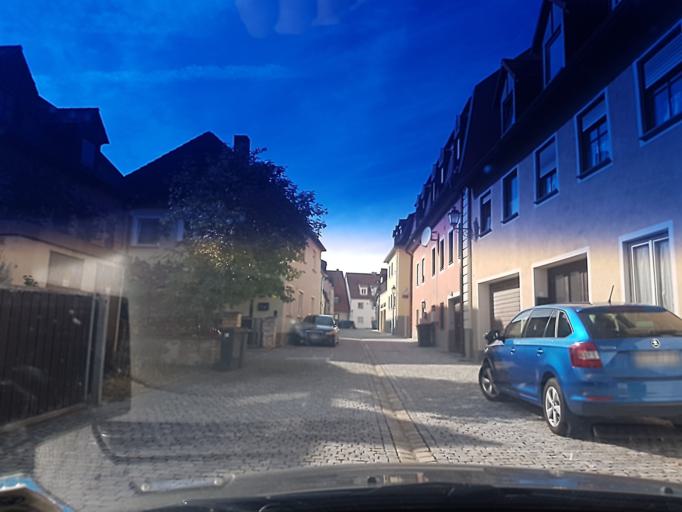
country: DE
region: Bavaria
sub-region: Upper Franconia
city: Schlusselfeld
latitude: 49.7564
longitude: 10.6189
